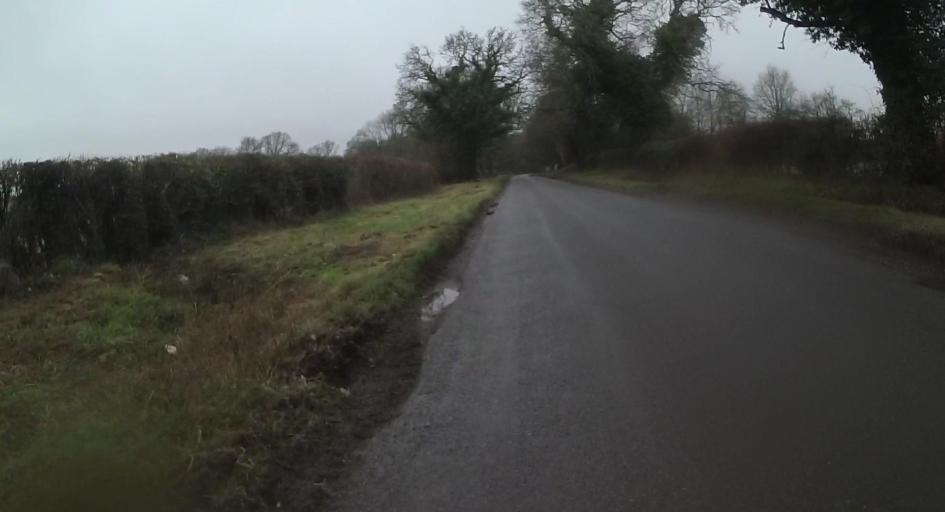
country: GB
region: England
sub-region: Hampshire
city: Kings Worthy
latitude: 51.1251
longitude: -1.2290
